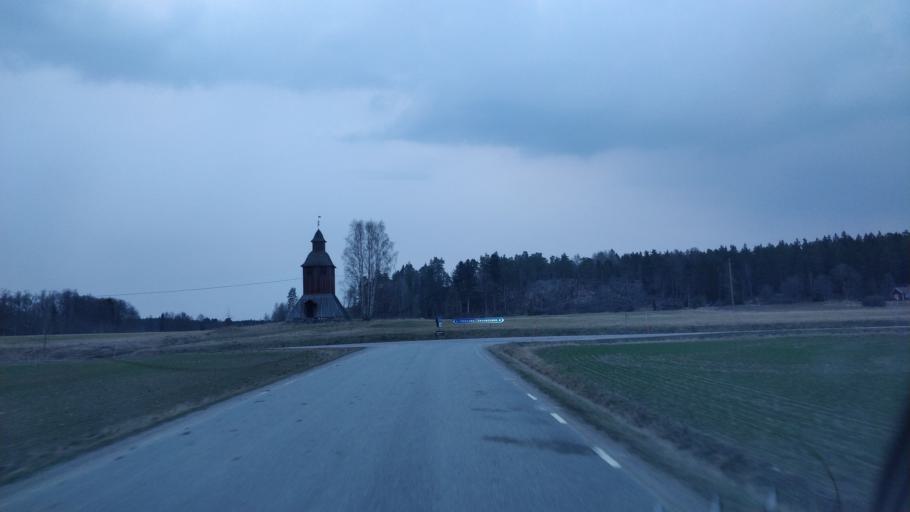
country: SE
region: Uppsala
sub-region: Enkopings Kommun
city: Orsundsbro
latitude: 59.7514
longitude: 17.1742
